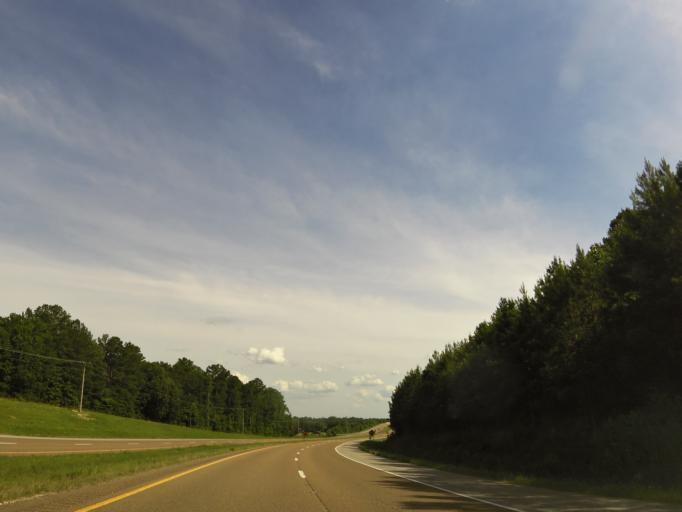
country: US
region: Tennessee
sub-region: Carroll County
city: Huntingdon
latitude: 36.0189
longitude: -88.3951
